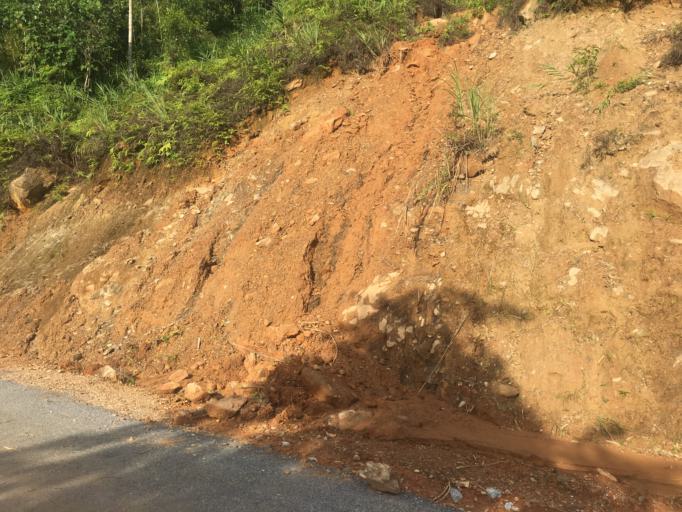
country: VN
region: Ha Giang
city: Thi Tran Tam Son
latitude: 22.9471
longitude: 105.0256
